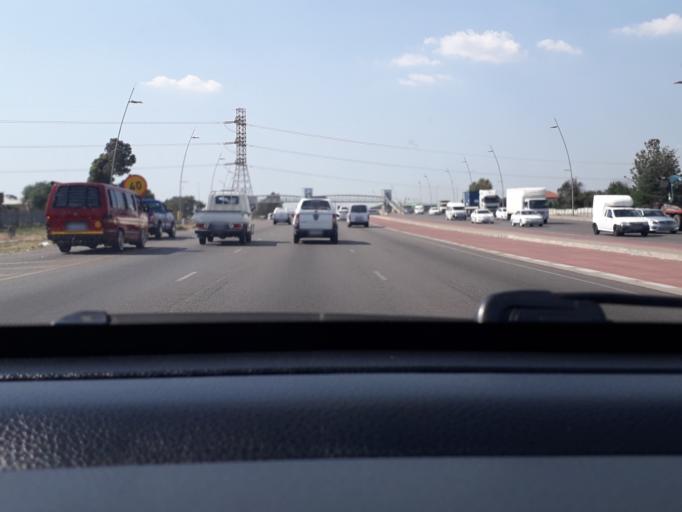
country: ZA
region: Gauteng
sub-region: City of Johannesburg Metropolitan Municipality
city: Modderfontein
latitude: -26.0823
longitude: 28.1896
